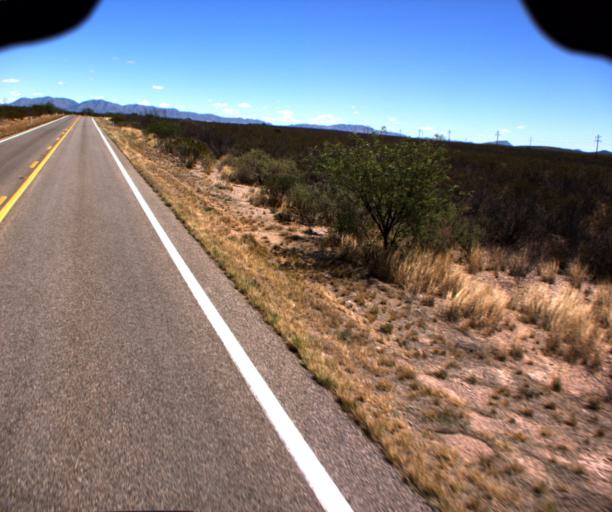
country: US
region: Arizona
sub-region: Cochise County
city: Tombstone
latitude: 31.7425
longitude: -110.1547
